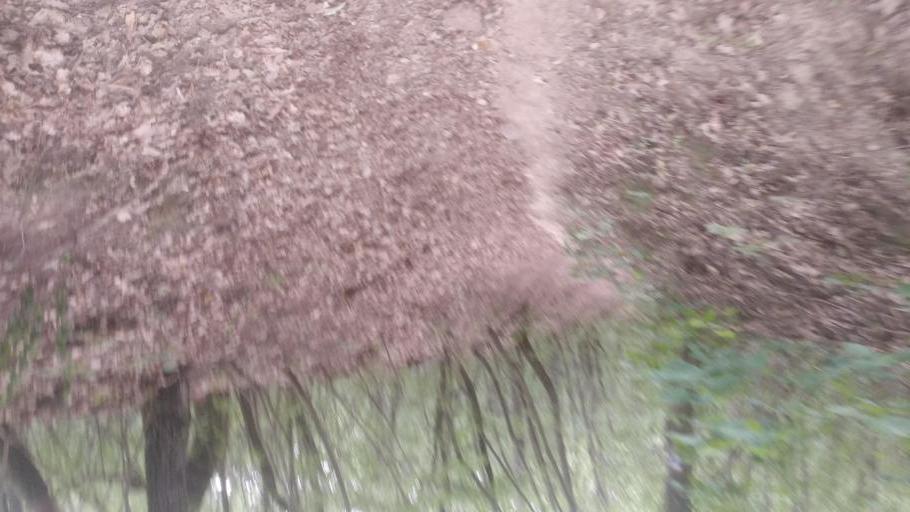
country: HU
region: Veszprem
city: Balatonalmadi
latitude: 47.0053
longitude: 17.9786
